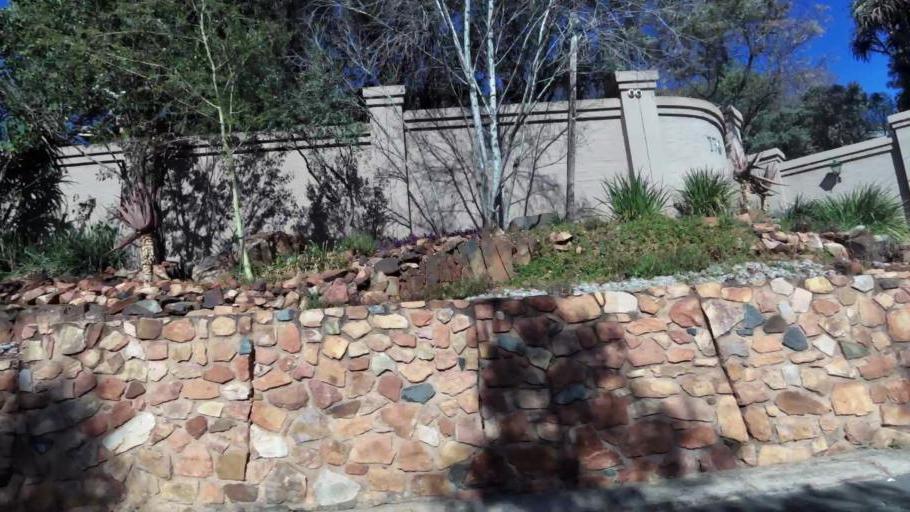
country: ZA
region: Gauteng
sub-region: City of Johannesburg Metropolitan Municipality
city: Roodepoort
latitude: -26.1436
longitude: 27.9656
